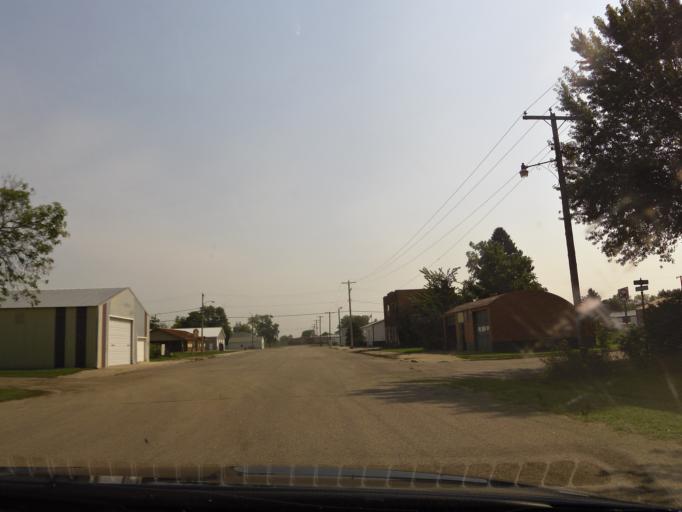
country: US
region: North Dakota
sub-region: Ransom County
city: Sheldon
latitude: 46.2666
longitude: -97.1325
